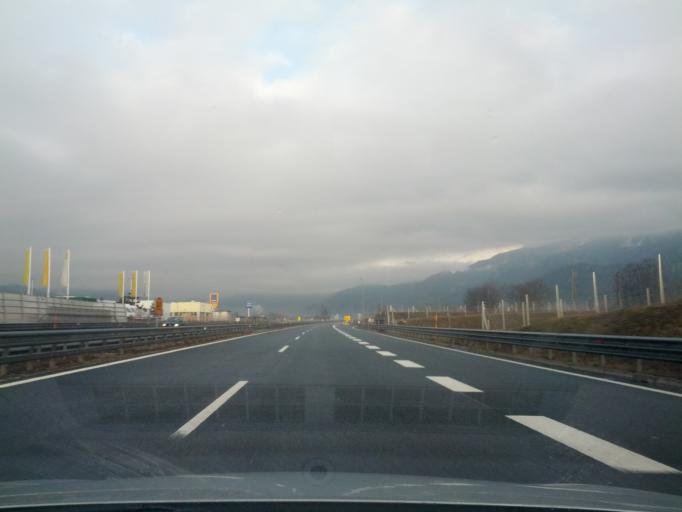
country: SI
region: Radovljica
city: Lesce
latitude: 46.3650
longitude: 14.1635
